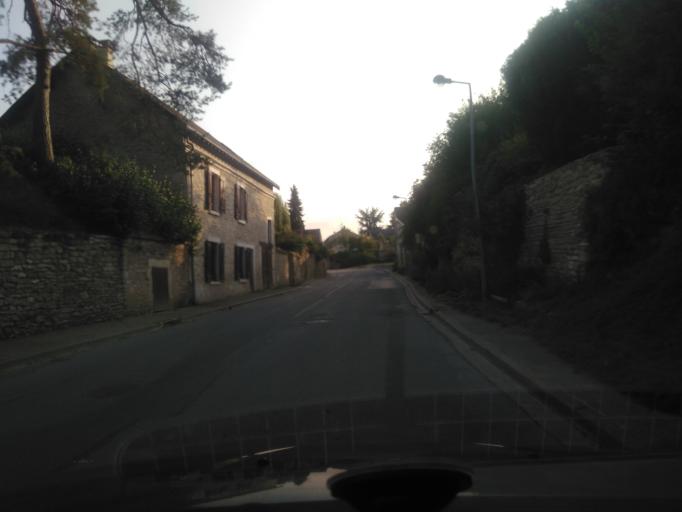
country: FR
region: Champagne-Ardenne
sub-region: Departement de la Marne
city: Fismes
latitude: 49.2702
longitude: 3.6984
